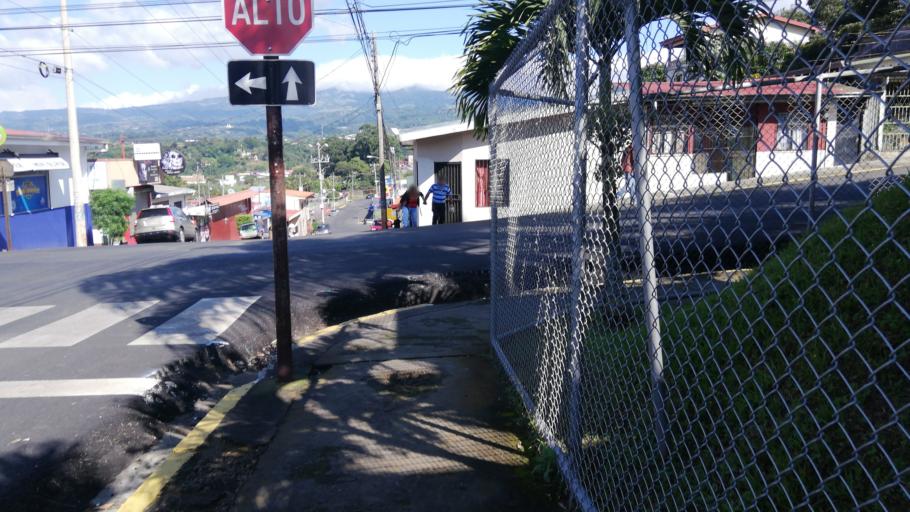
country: CR
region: Alajuela
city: San Juan
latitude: 10.0744
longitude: -84.3098
